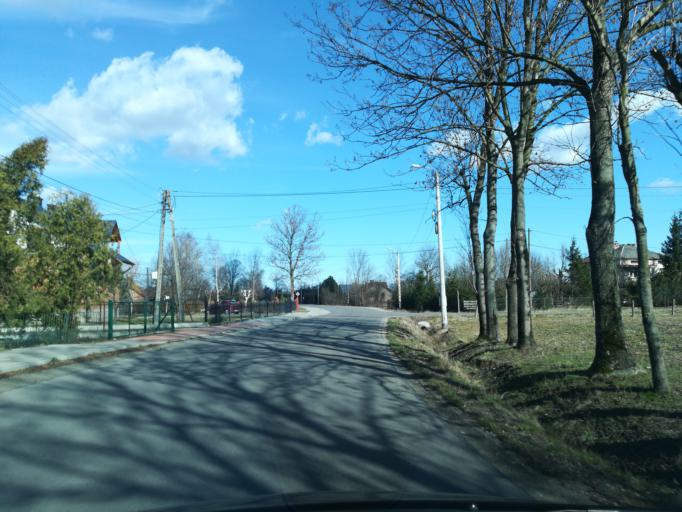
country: PL
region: Subcarpathian Voivodeship
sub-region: Powiat lancucki
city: Bialobrzegi
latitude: 50.0987
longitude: 22.3187
